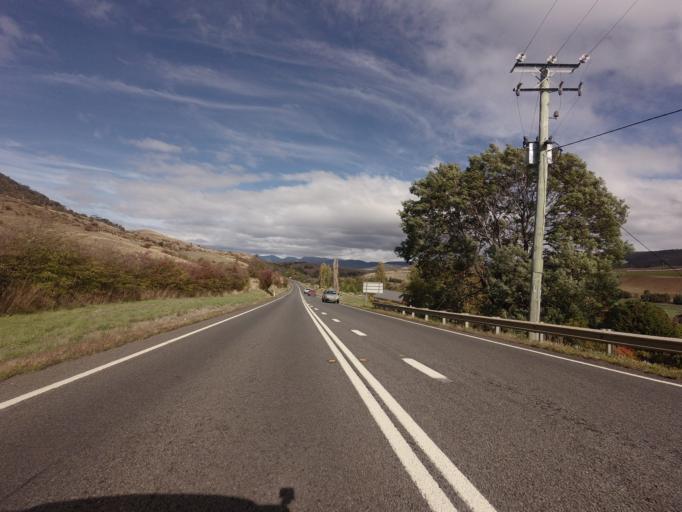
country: AU
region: Tasmania
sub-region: Derwent Valley
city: New Norfolk
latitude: -42.7222
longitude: 146.9497
